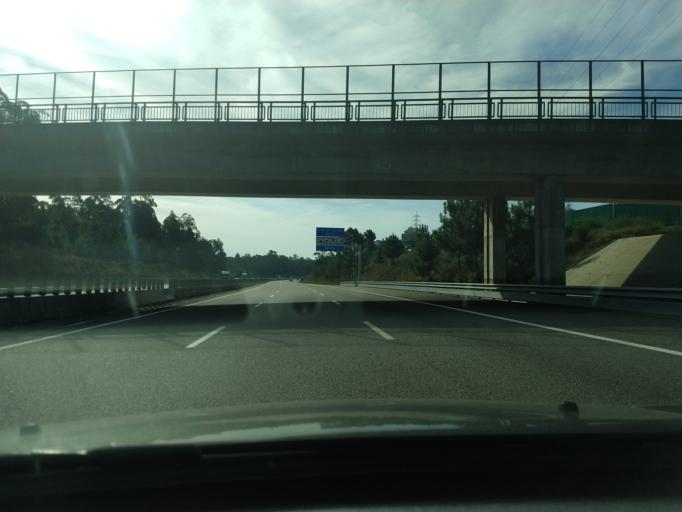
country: PT
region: Aveiro
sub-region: Ovar
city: Valega
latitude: 40.8455
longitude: -8.5572
